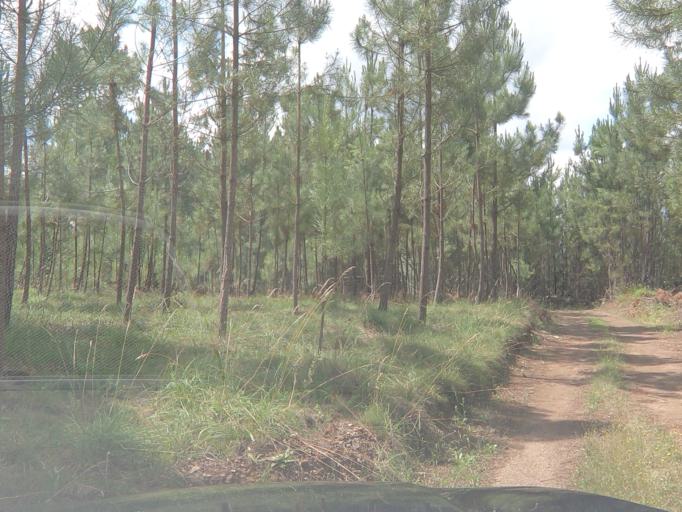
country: PT
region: Vila Real
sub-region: Sabrosa
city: Vilela
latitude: 41.2669
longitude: -7.6669
